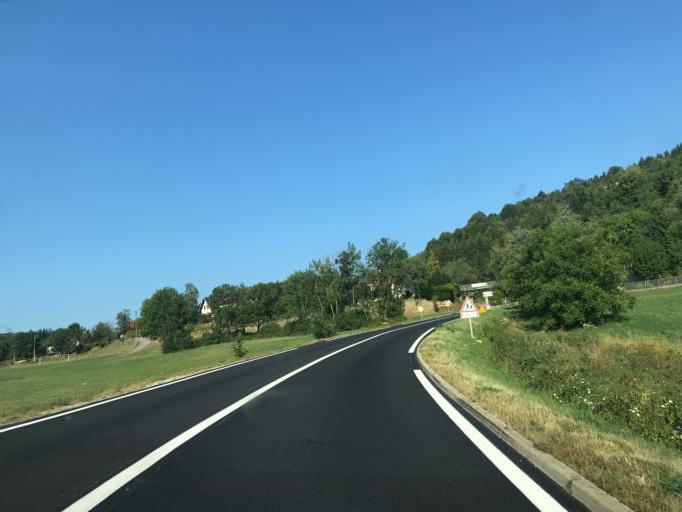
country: FR
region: Franche-Comte
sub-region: Departement du Jura
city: Lavans-les-Saint-Claude
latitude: 46.3760
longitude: 5.7637
